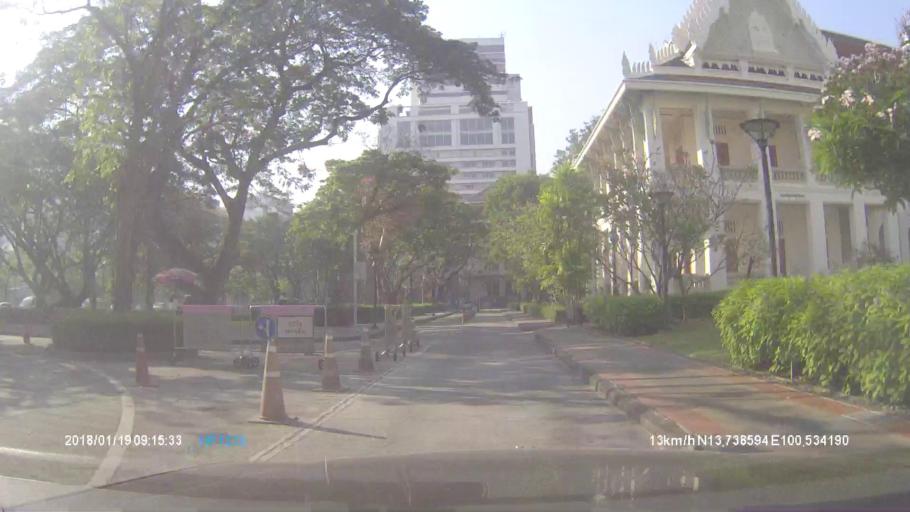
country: TH
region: Bangkok
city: Pathum Wan
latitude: 13.7384
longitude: 100.5341
